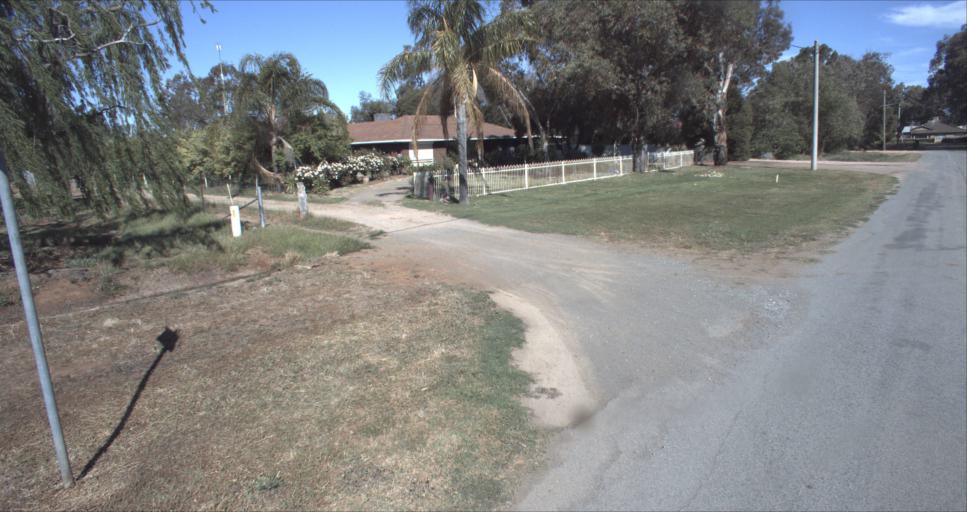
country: AU
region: New South Wales
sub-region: Leeton
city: Leeton
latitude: -34.5588
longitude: 146.3882
